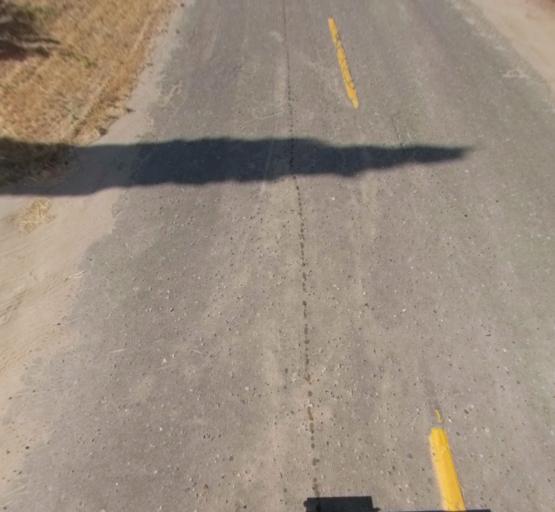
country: US
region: California
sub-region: Madera County
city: Chowchilla
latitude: 37.0850
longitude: -120.2613
